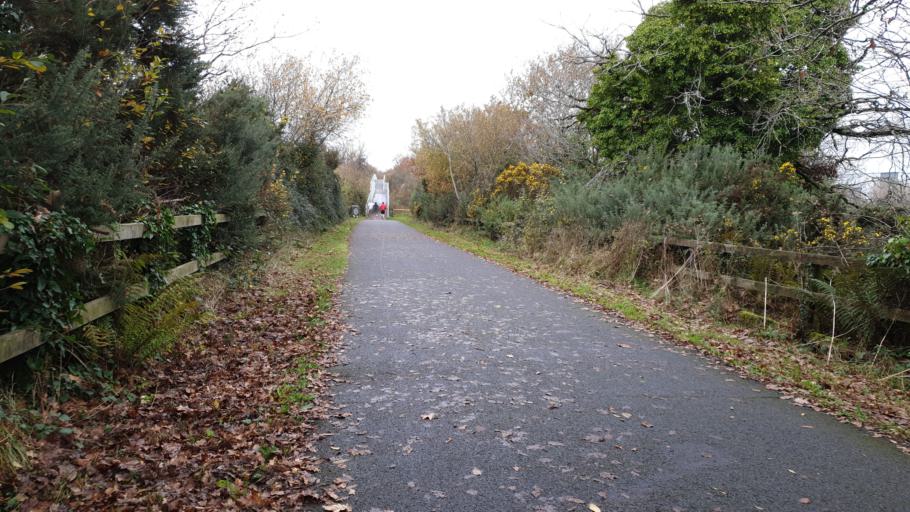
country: IE
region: Munster
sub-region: County Cork
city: Passage West
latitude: 51.8815
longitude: -8.4021
